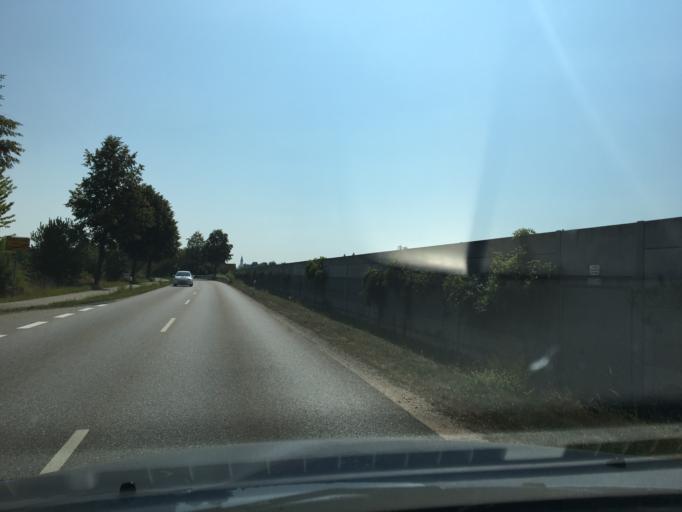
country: DE
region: Bavaria
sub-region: Upper Bavaria
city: Mettenheim
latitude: 48.2505
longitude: 12.4730
